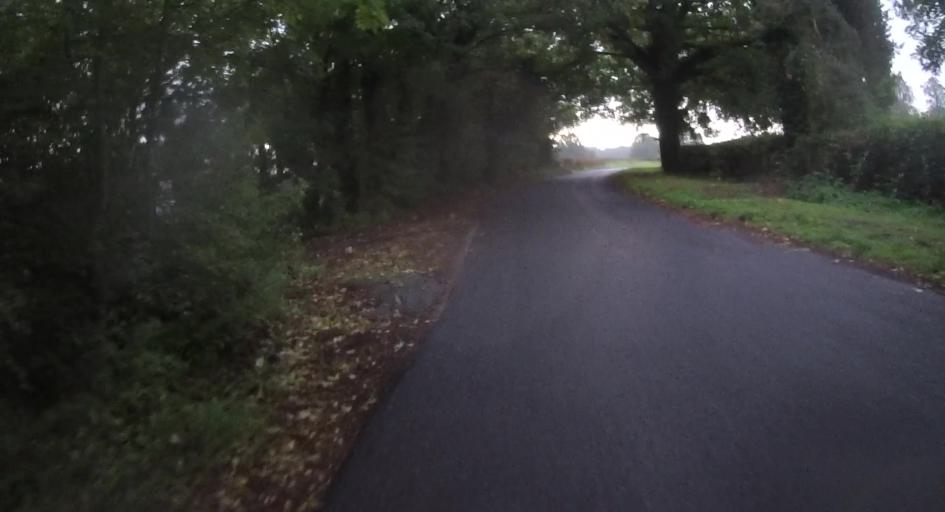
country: GB
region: England
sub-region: Hampshire
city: Tadley
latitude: 51.3213
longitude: -1.1496
